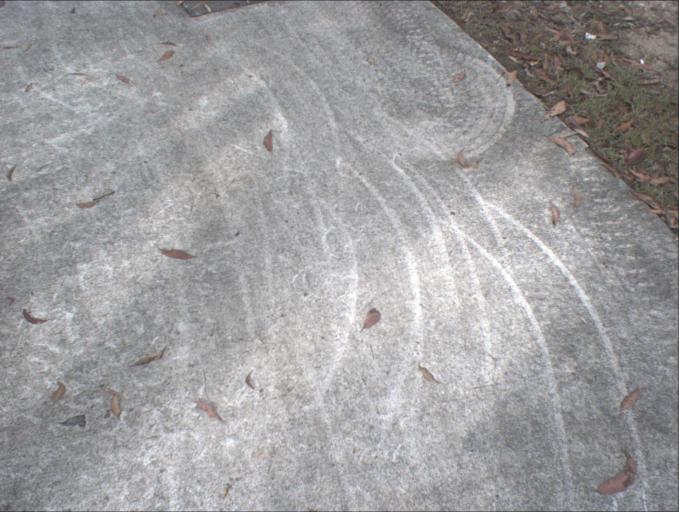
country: AU
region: Queensland
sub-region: Logan
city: Logan Reserve
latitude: -27.6969
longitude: 153.0772
